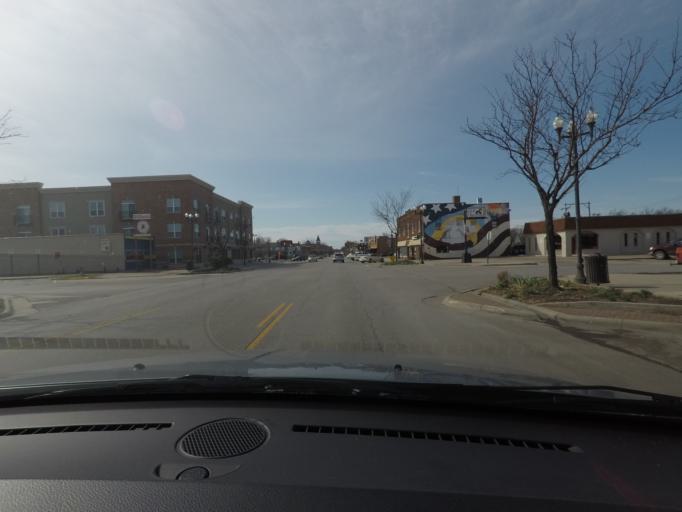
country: US
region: Kansas
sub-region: Lyon County
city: Emporia
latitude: 38.4113
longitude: -96.1802
